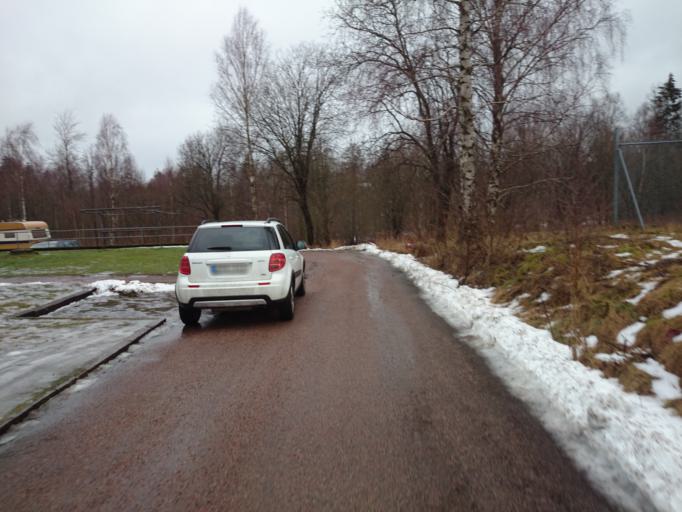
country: SE
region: Halland
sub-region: Hylte Kommun
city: Hyltebruk
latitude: 57.0016
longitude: 13.2514
